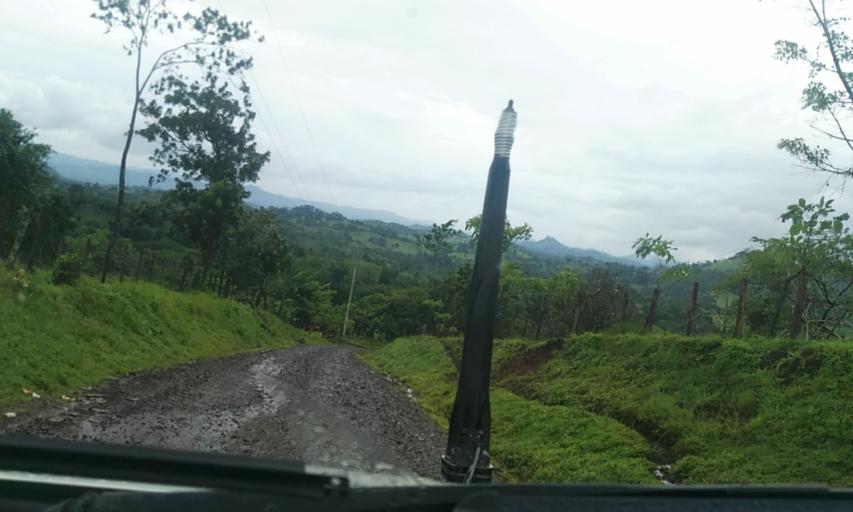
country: NI
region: Matagalpa
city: Rio Blanco
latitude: 13.0176
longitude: -85.2066
